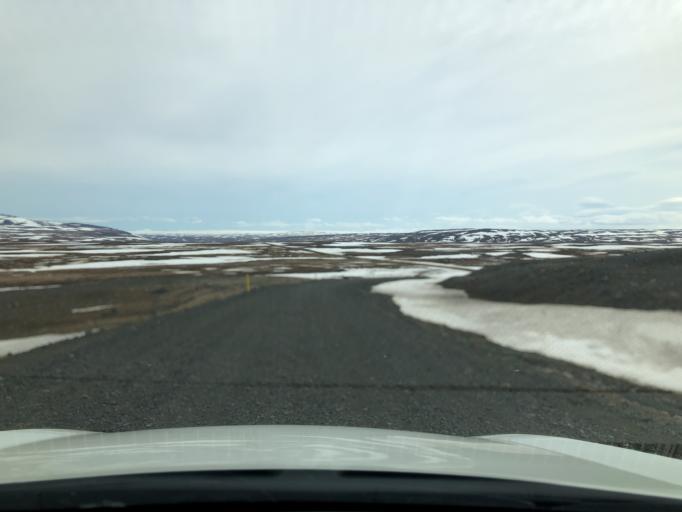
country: IS
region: East
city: Egilsstadir
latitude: 65.3081
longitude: -15.3595
